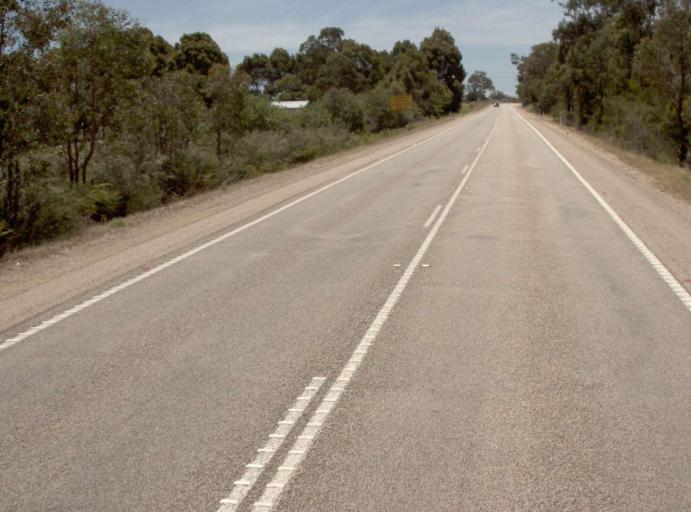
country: AU
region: Victoria
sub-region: East Gippsland
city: Bairnsdale
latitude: -37.7838
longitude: 147.6819
